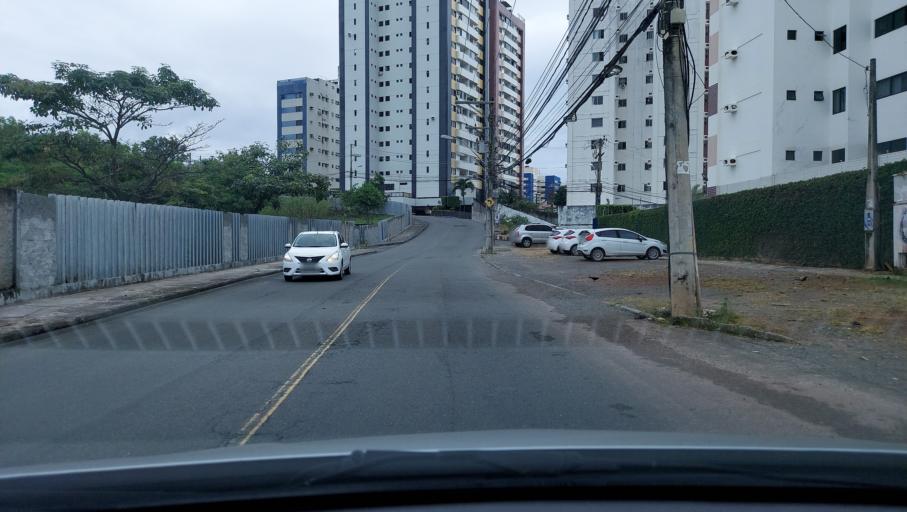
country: BR
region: Bahia
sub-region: Salvador
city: Salvador
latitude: -12.9834
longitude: -38.4423
